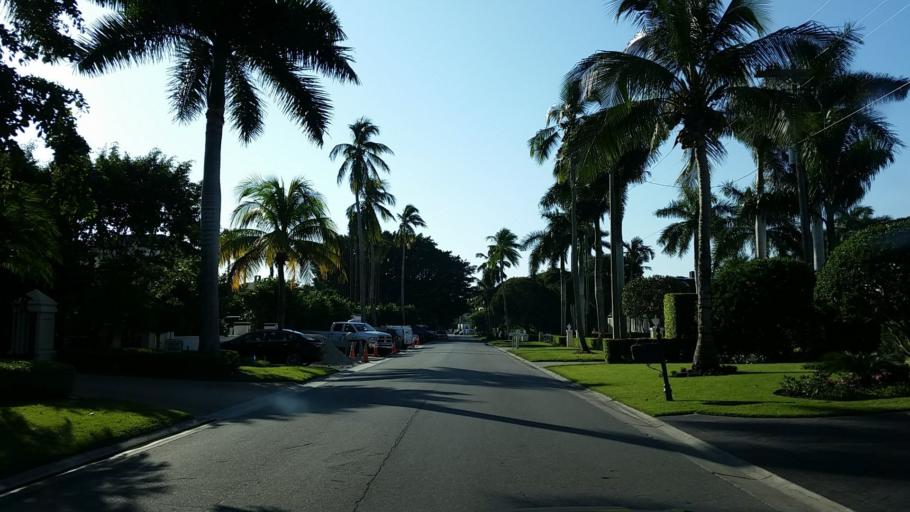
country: US
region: Florida
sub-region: Collier County
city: Naples
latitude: 26.1096
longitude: -81.7933
